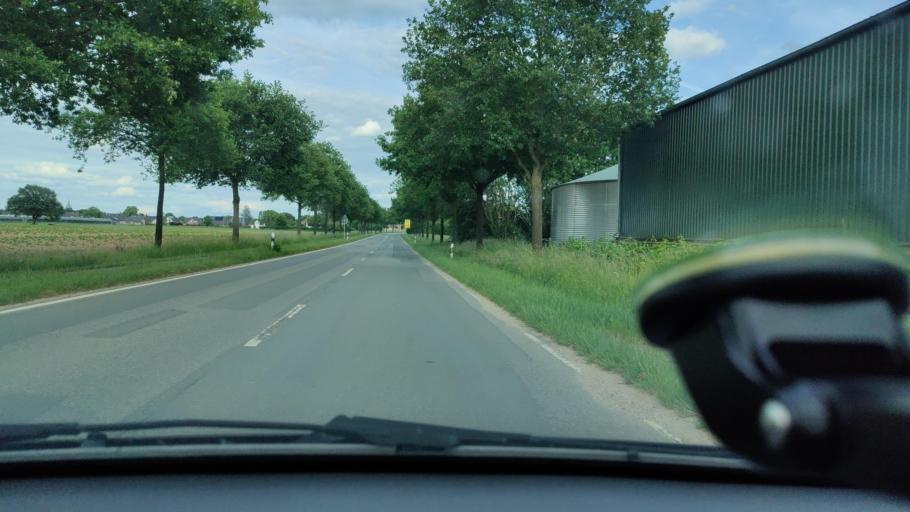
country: DE
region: North Rhine-Westphalia
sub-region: Regierungsbezirk Dusseldorf
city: Weeze
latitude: 51.6234
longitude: 6.1774
